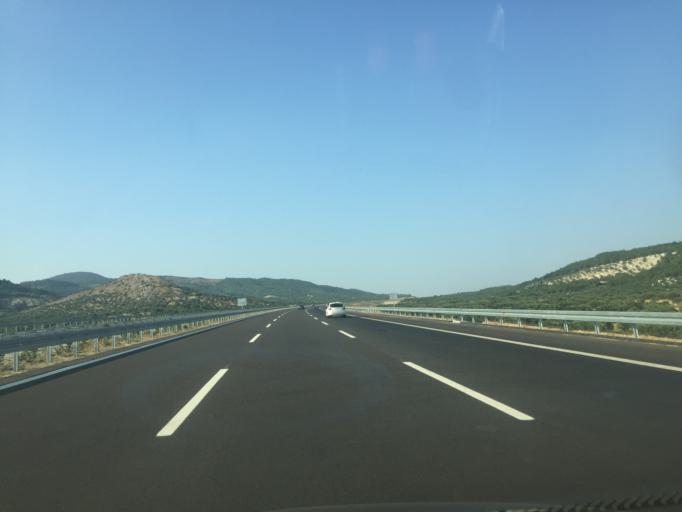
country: TR
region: Manisa
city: Zeytinliova
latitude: 38.9845
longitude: 27.7317
